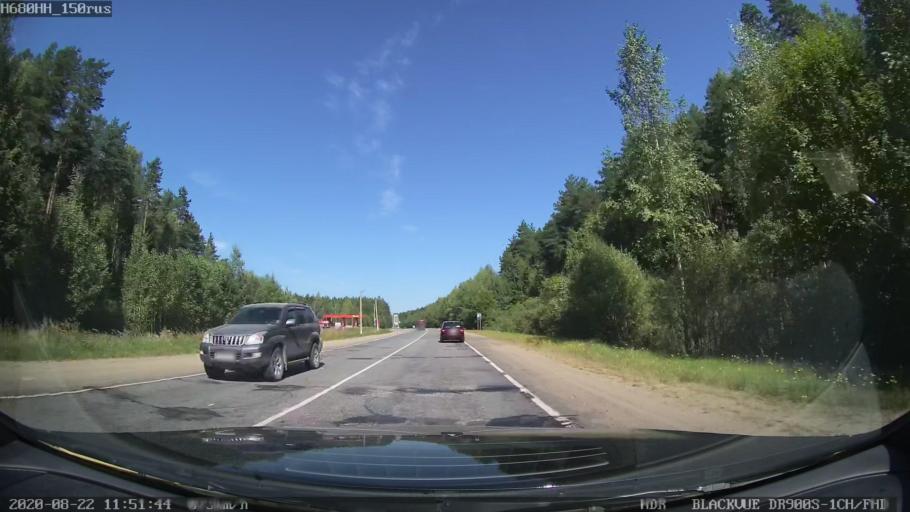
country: RU
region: Tverskaya
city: Sakharovo
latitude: 57.1070
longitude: 36.1205
